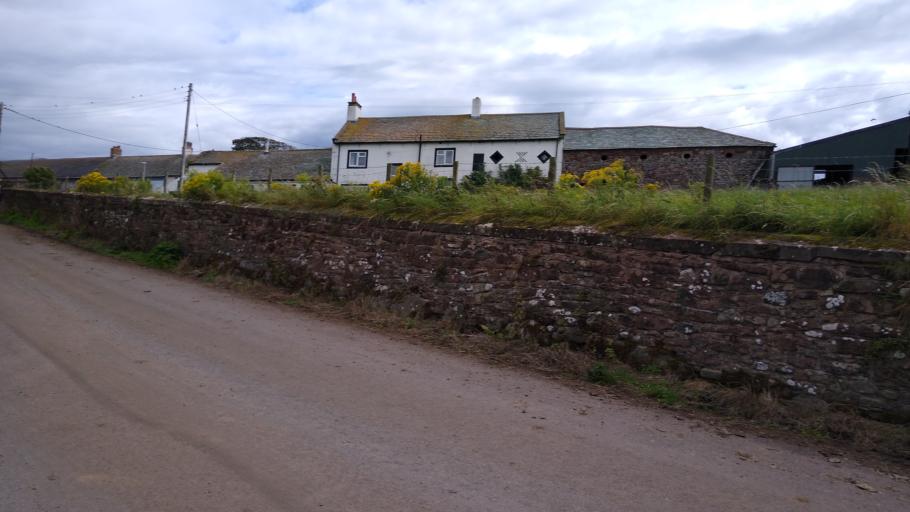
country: GB
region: England
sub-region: Cumbria
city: Silloth
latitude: 54.7966
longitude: -3.4016
